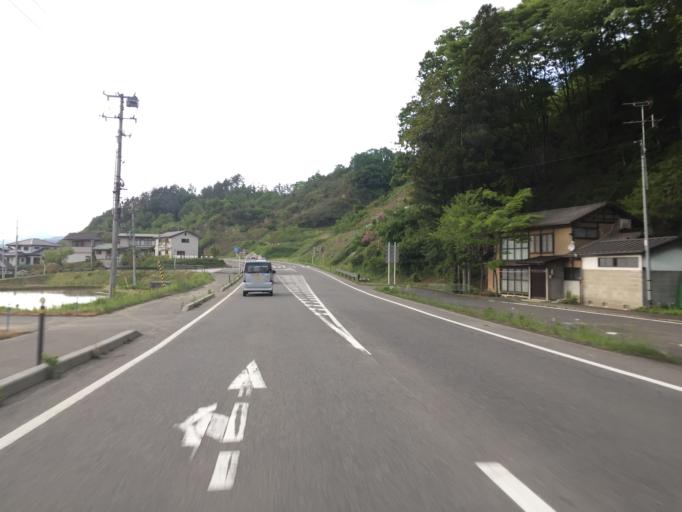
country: JP
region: Fukushima
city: Fukushima-shi
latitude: 37.6497
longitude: 140.6128
